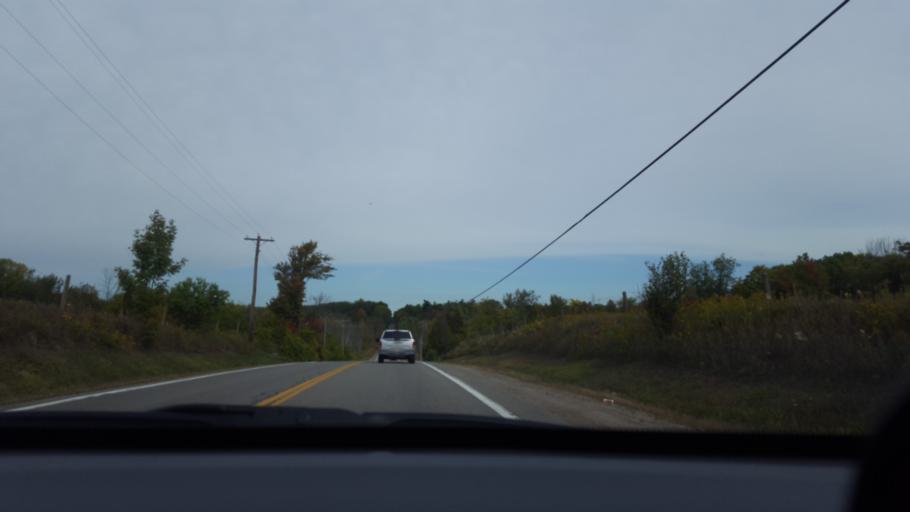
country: CA
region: Ontario
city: Vaughan
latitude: 43.9492
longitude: -79.5338
